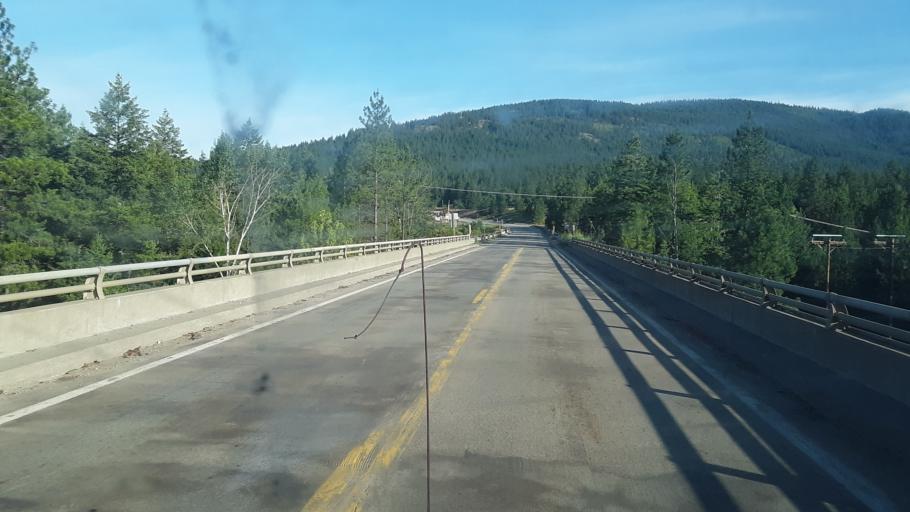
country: US
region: Idaho
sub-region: Boundary County
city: Bonners Ferry
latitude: 48.7294
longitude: -116.1792
